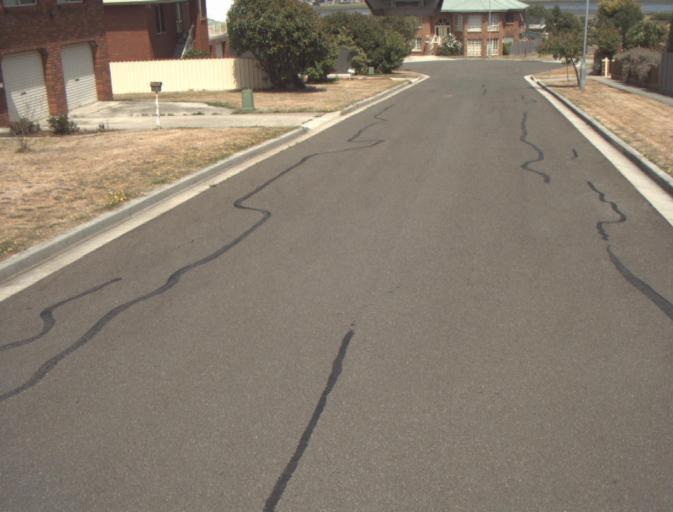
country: AU
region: Tasmania
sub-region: Launceston
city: Mayfield
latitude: -41.3795
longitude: 147.1189
